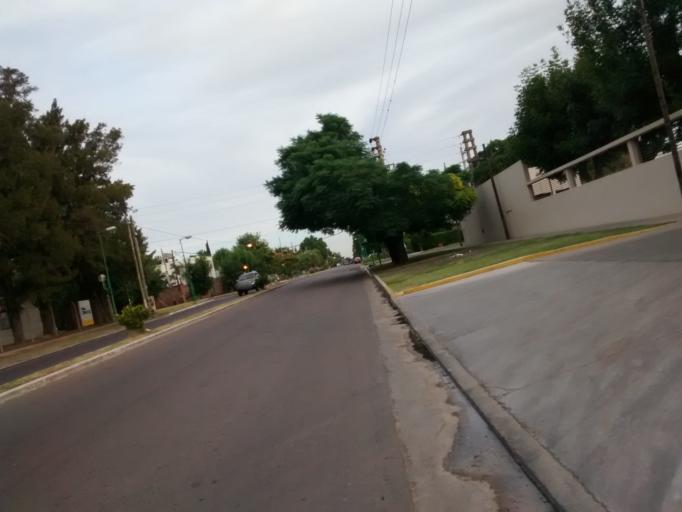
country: AR
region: Buenos Aires
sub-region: Partido de La Plata
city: La Plata
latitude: -34.9024
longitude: -58.0214
